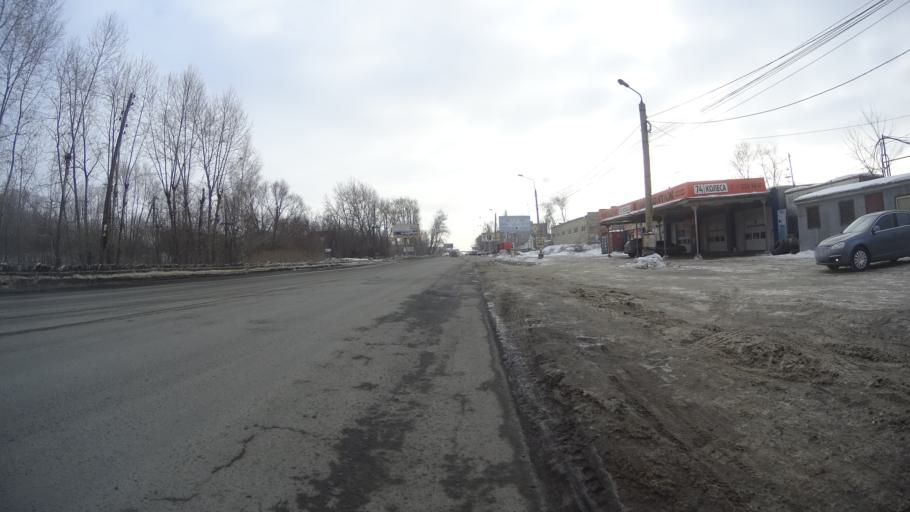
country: RU
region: Chelyabinsk
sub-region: Gorod Chelyabinsk
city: Chelyabinsk
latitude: 55.1250
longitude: 61.3858
